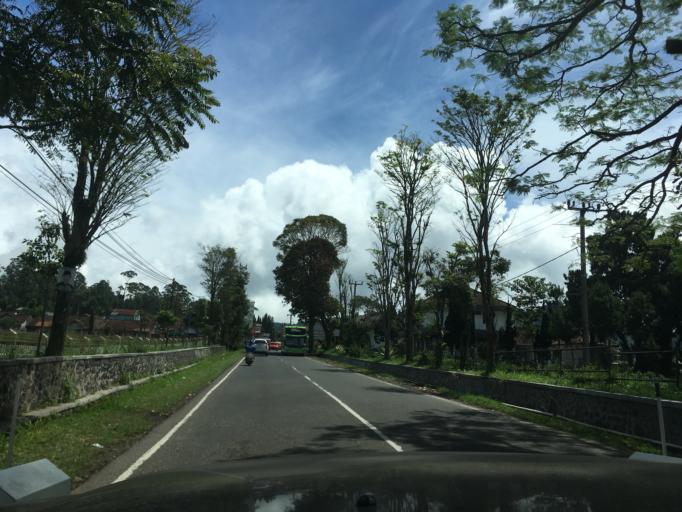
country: ID
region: West Java
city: Lembang
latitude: -6.7995
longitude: 107.6521
